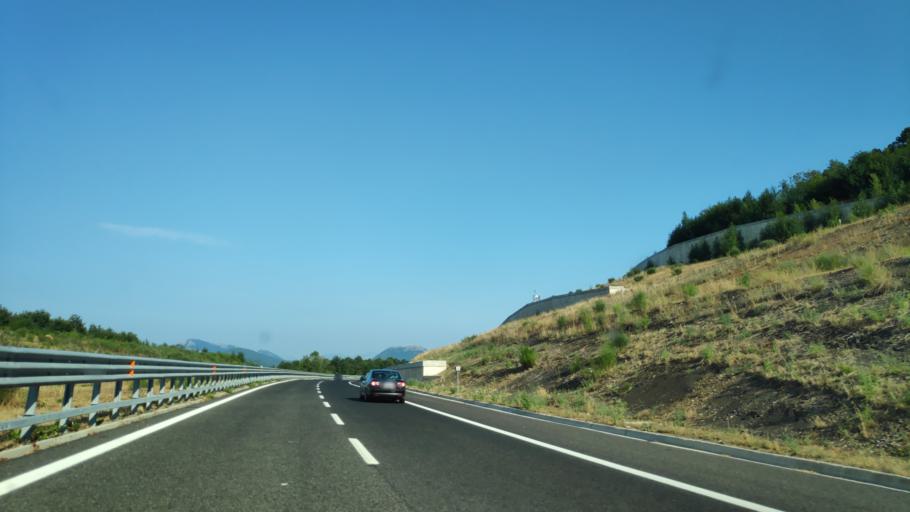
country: IT
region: Basilicate
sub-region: Provincia di Potenza
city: Nemoli
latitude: 40.1014
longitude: 15.8004
